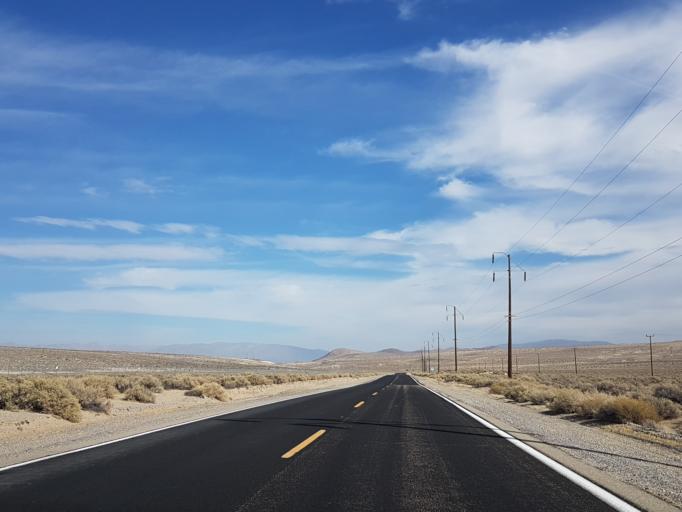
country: US
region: California
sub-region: San Bernardino County
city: Searles Valley
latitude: 35.6487
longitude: -117.4879
